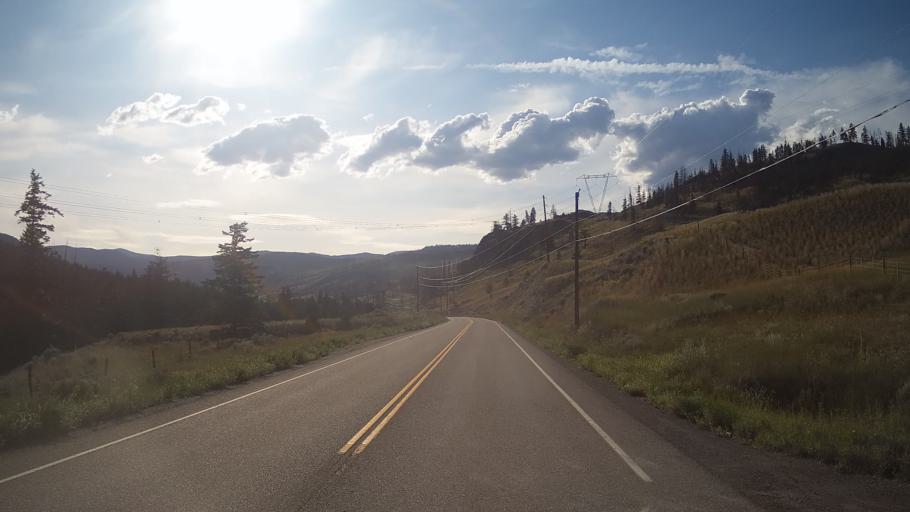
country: CA
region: British Columbia
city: Cache Creek
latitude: 50.8850
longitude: -121.4305
